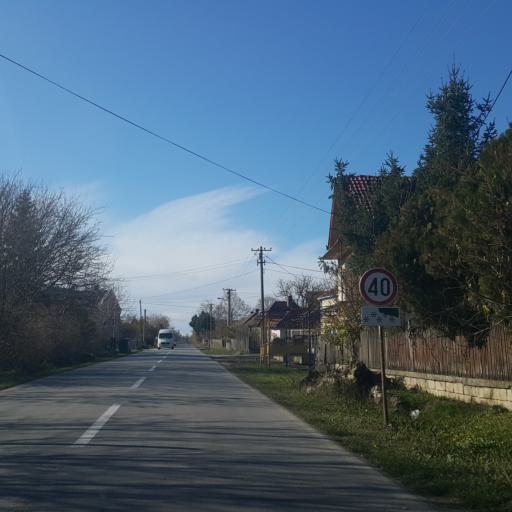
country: RS
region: Central Serbia
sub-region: Sumadijski Okrug
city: Topola
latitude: 44.2521
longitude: 20.7974
